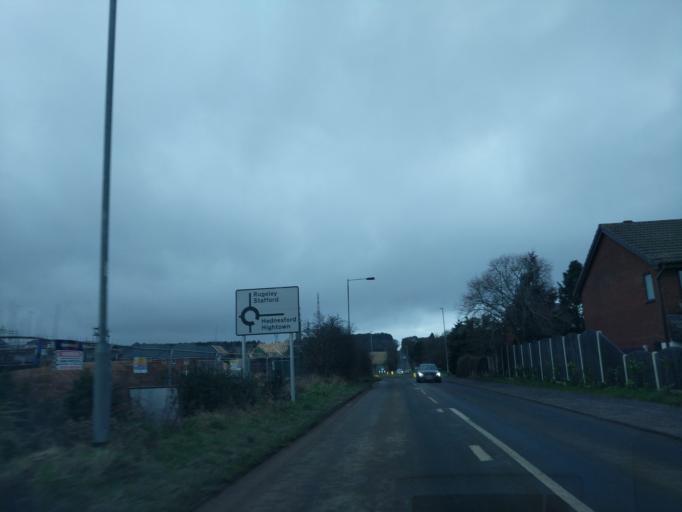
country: GB
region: England
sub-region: Staffordshire
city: Cannock
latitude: 52.7207
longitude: -2.0205
